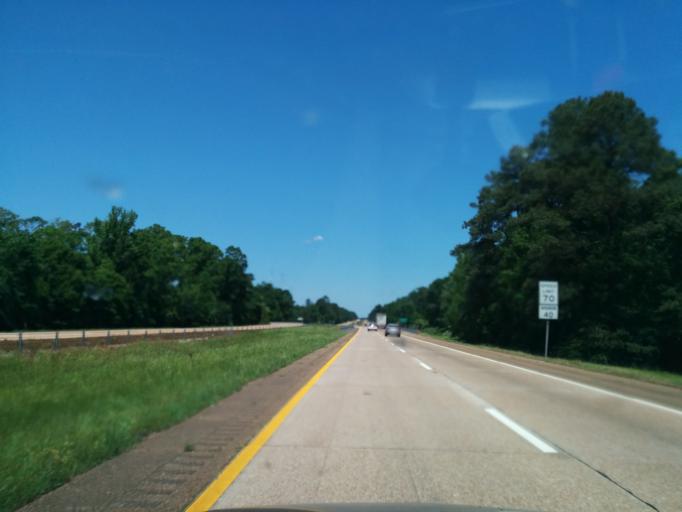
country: US
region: Mississippi
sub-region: Pike County
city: Magnolia
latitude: 31.1188
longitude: -90.4840
